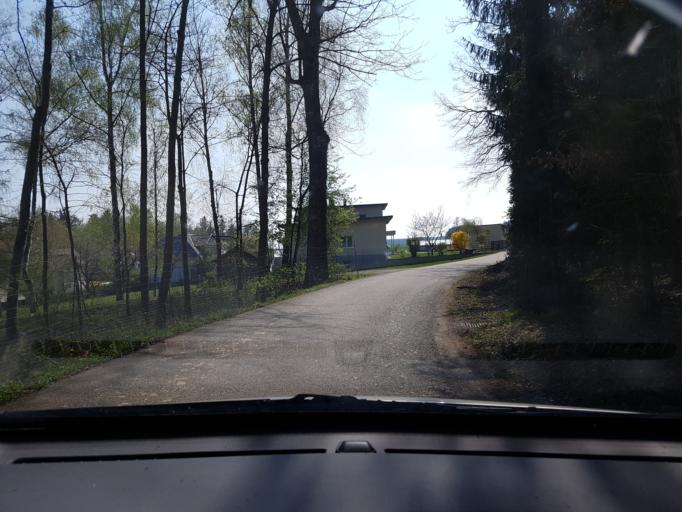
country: AT
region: Upper Austria
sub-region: Politischer Bezirk Linz-Land
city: Ansfelden
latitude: 48.1654
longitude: 14.3207
